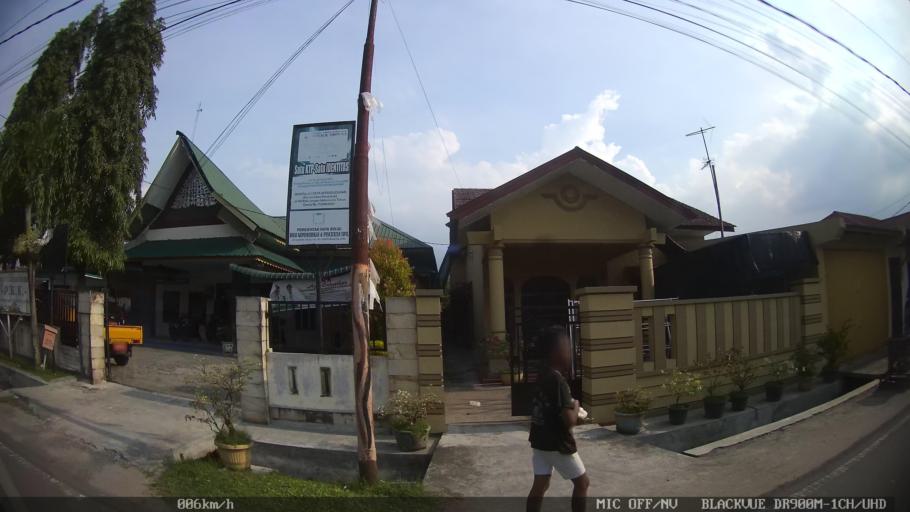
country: ID
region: North Sumatra
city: Binjai
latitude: 3.6029
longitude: 98.4985
